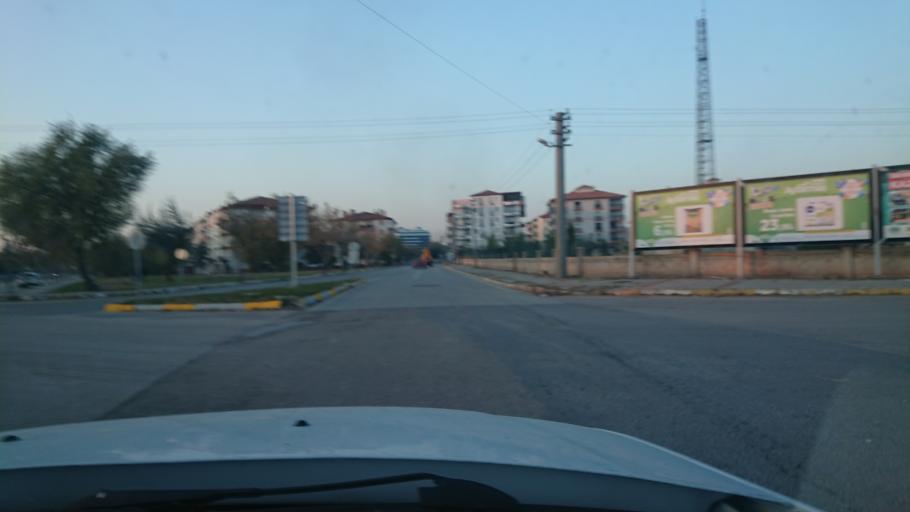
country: TR
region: Aksaray
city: Aksaray
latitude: 38.3526
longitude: 34.0427
